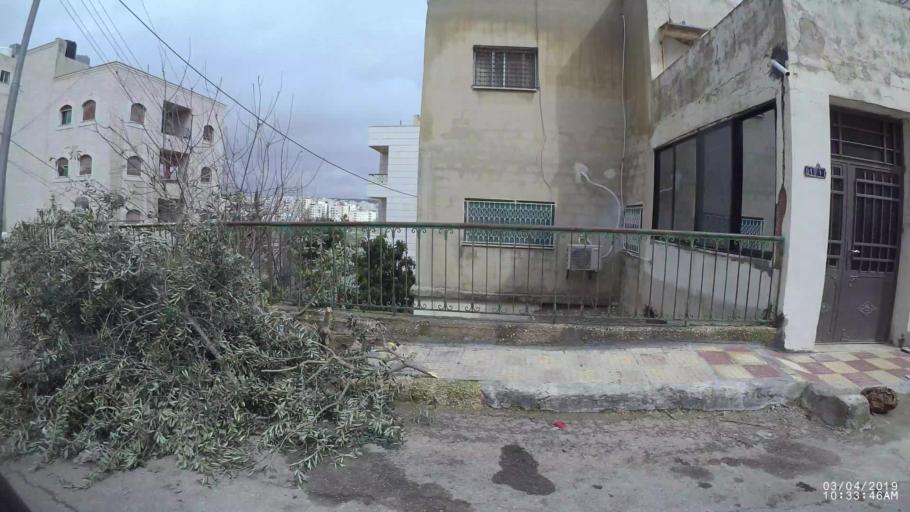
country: JO
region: Amman
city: Wadi as Sir
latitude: 31.9545
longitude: 35.8305
